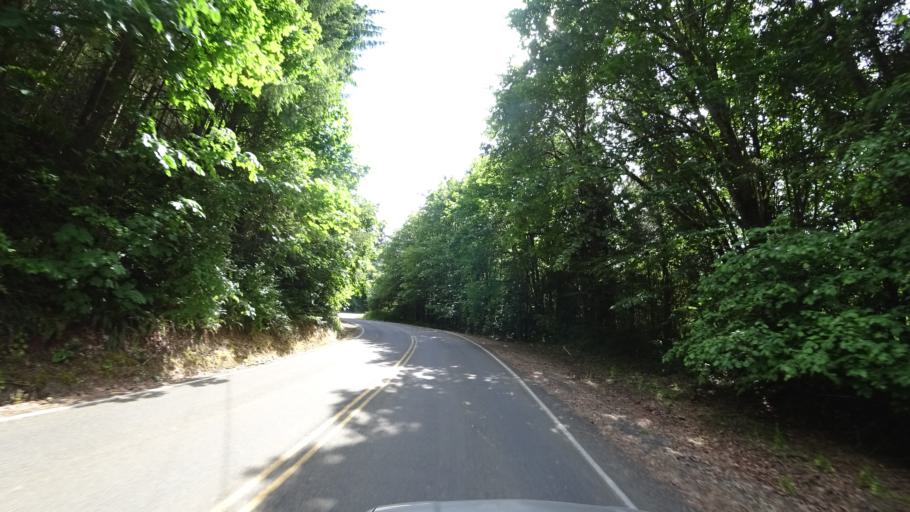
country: US
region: Oregon
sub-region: Washington County
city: Bethany
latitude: 45.6146
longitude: -122.8165
